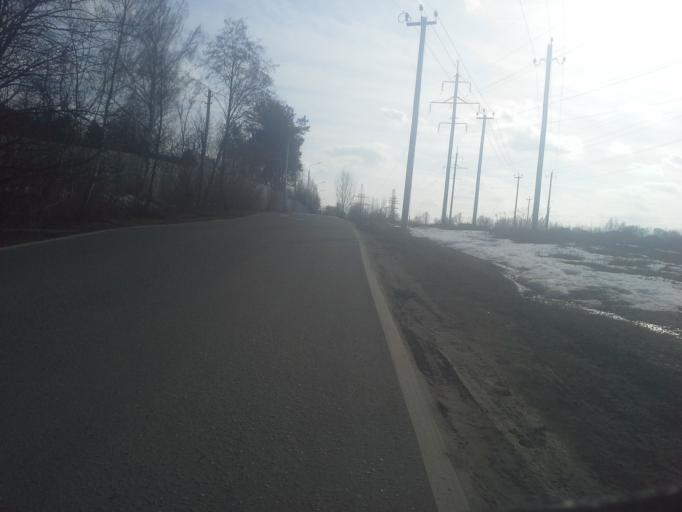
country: RU
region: Moskovskaya
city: Dubrovitsy
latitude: 55.4617
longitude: 37.5200
